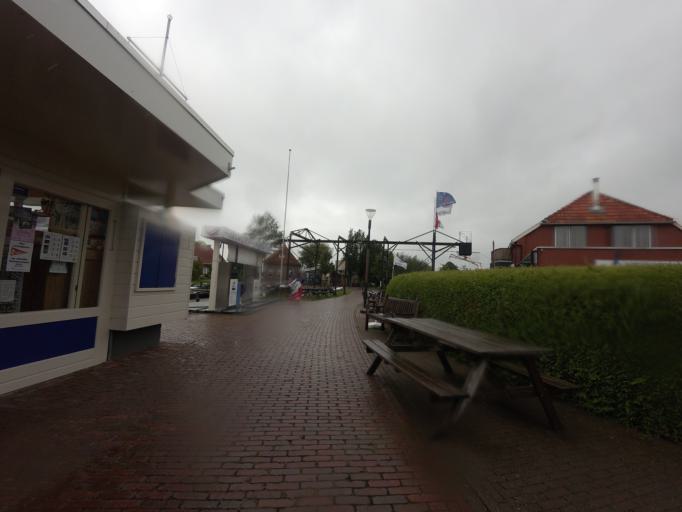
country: NL
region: Friesland
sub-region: Gemeente Boarnsterhim
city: Warten
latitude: 53.1292
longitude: 5.9390
